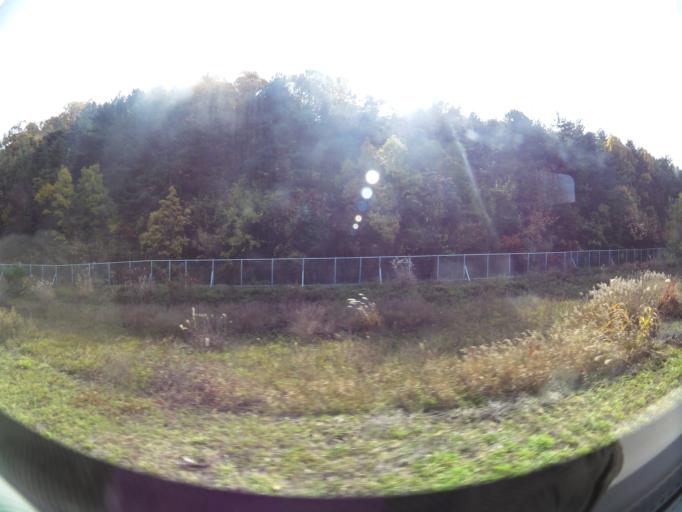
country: KR
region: Daejeon
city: Daejeon
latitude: 36.3383
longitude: 127.4946
